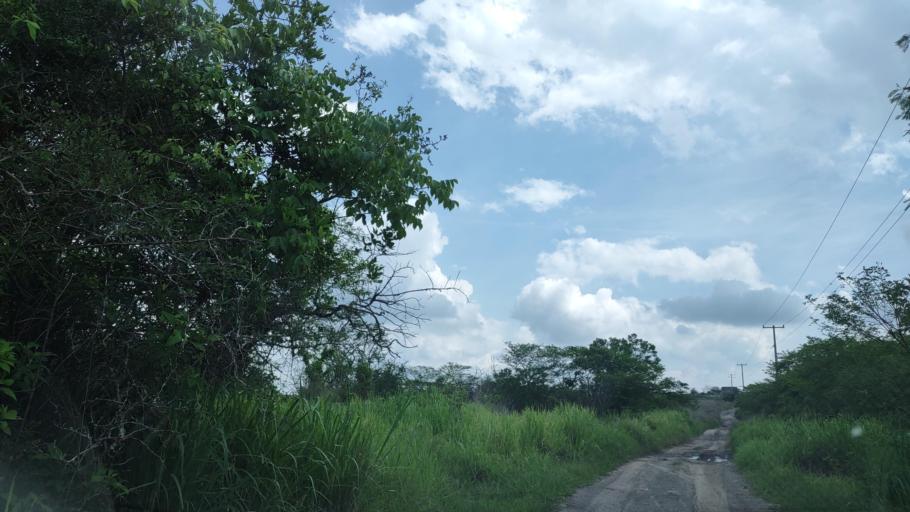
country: MX
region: Veracruz
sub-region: Emiliano Zapata
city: Dos Rios
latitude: 19.4559
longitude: -96.8084
